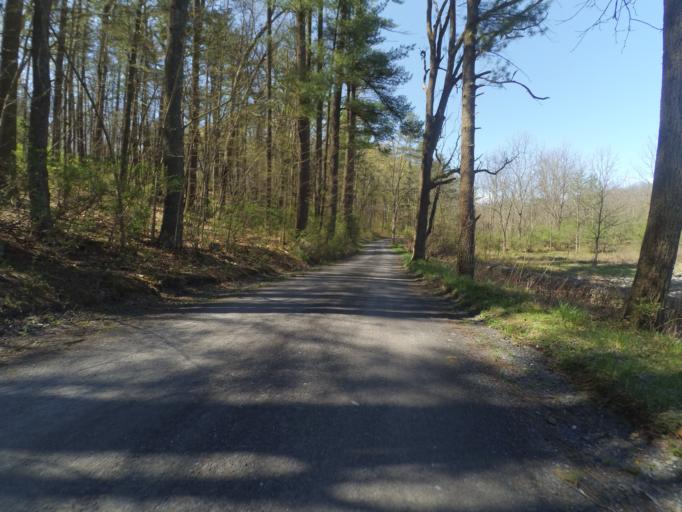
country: US
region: Pennsylvania
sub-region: Centre County
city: Houserville
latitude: 40.8361
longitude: -77.8435
